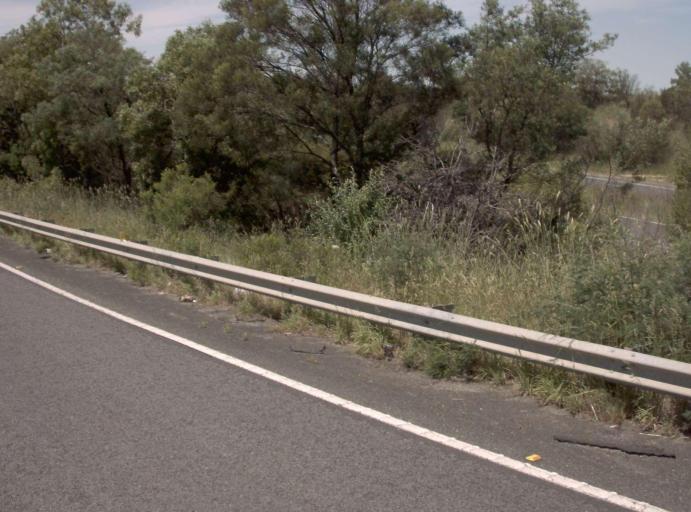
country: AU
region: Victoria
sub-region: Latrobe
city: Morwell
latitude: -38.2287
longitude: 146.4579
